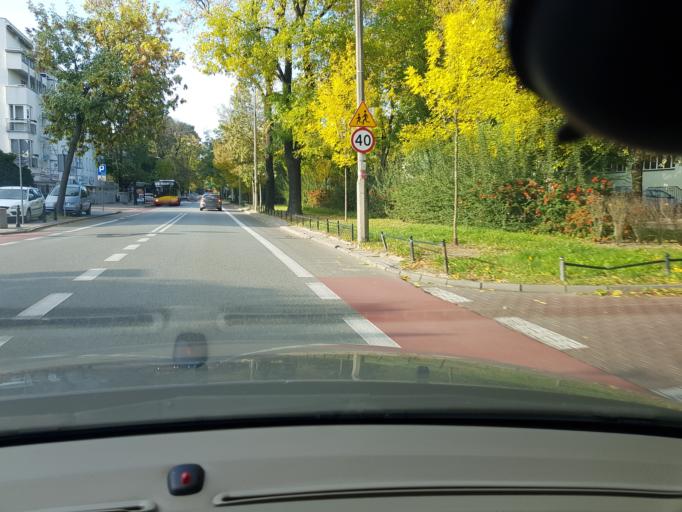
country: PL
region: Masovian Voivodeship
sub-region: Warszawa
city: Praga Poludnie
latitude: 52.2366
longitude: 21.0579
